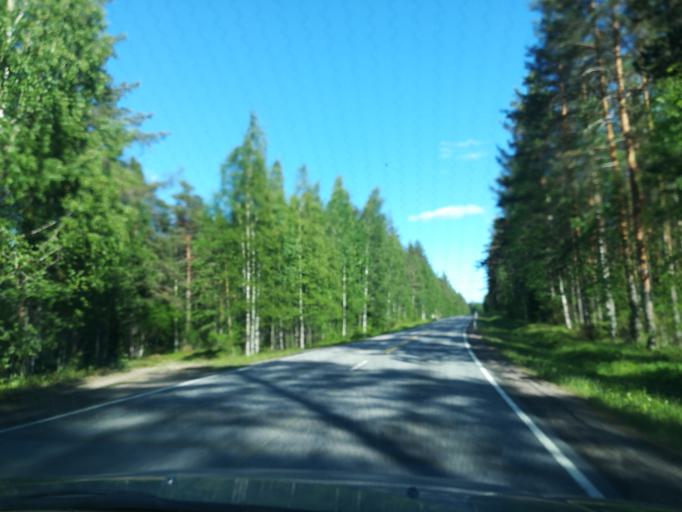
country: FI
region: South Karelia
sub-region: Imatra
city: Ruokolahti
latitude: 61.4023
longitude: 28.5954
